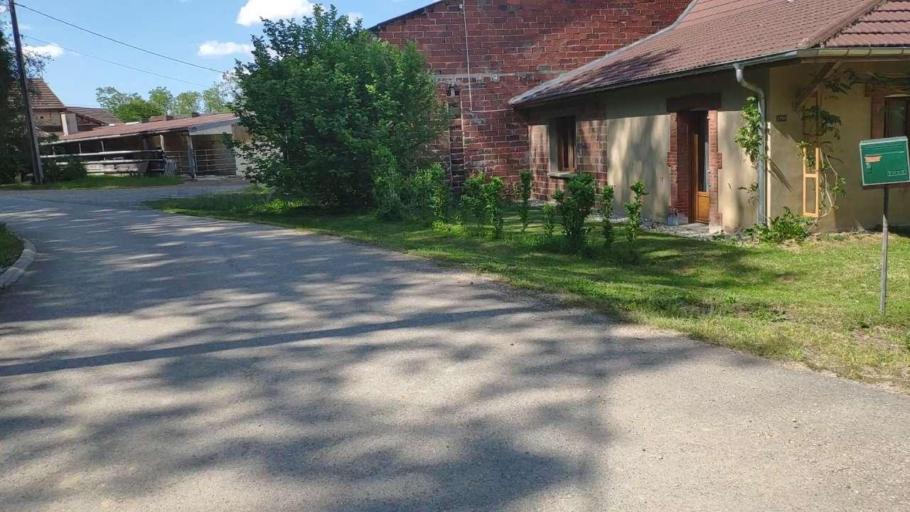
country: FR
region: Franche-Comte
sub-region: Departement du Jura
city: Bletterans
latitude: 46.8186
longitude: 5.4094
